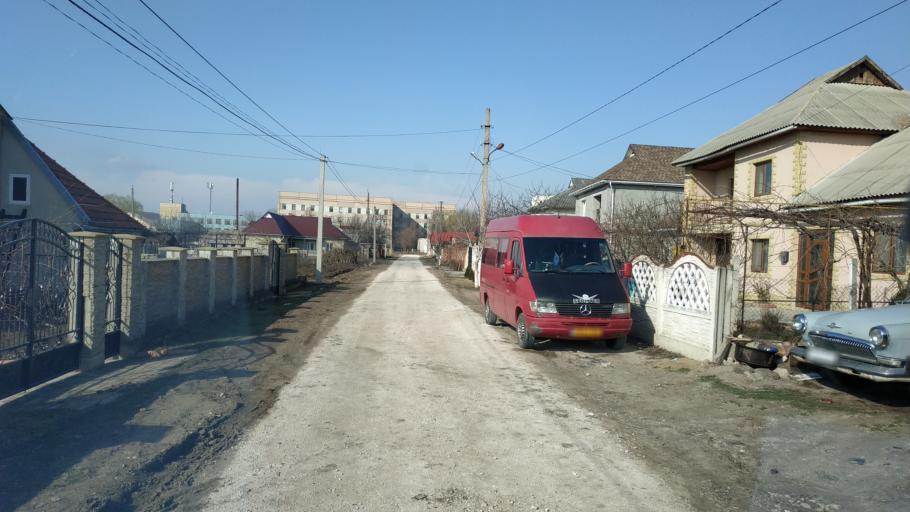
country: MD
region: Chisinau
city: Singera
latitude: 46.6848
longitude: 29.0611
